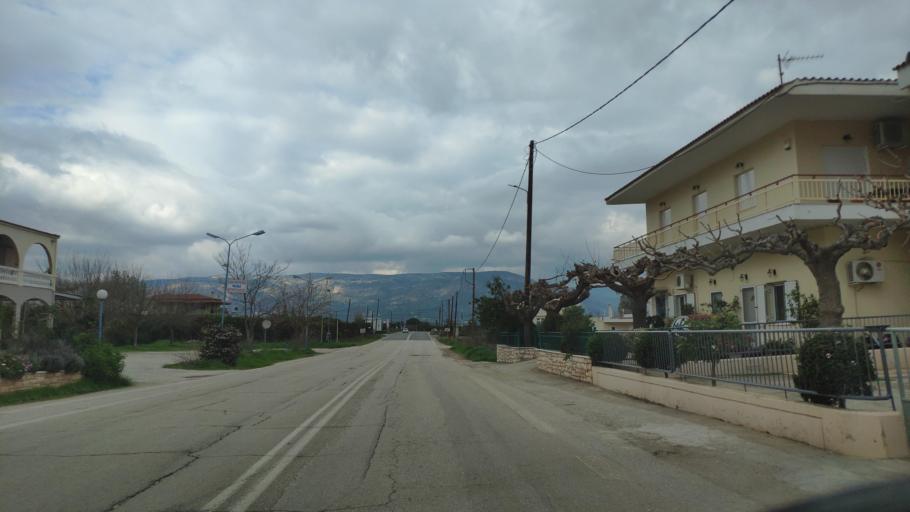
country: GR
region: Peloponnese
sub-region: Nomos Argolidos
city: Nea Kios
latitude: 37.5587
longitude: 22.7120
